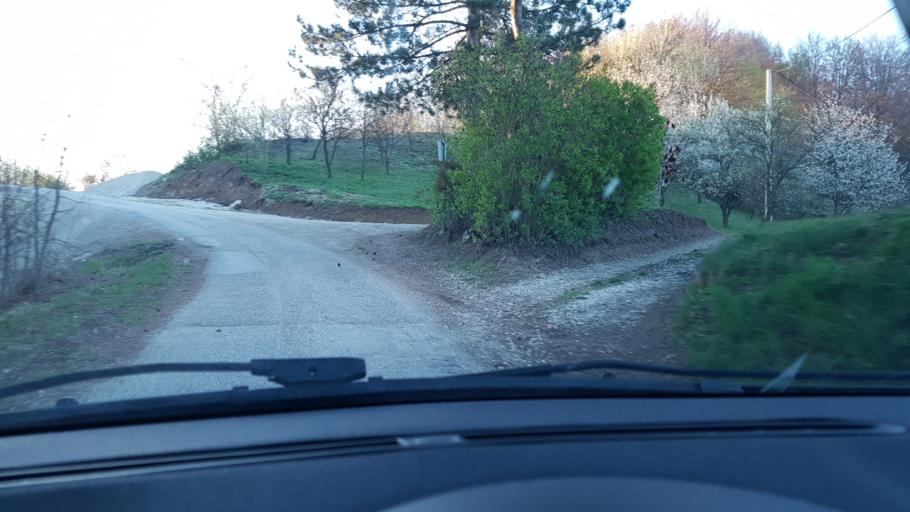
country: SI
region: Rogatec
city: Rogatec
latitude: 46.1742
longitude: 15.6853
